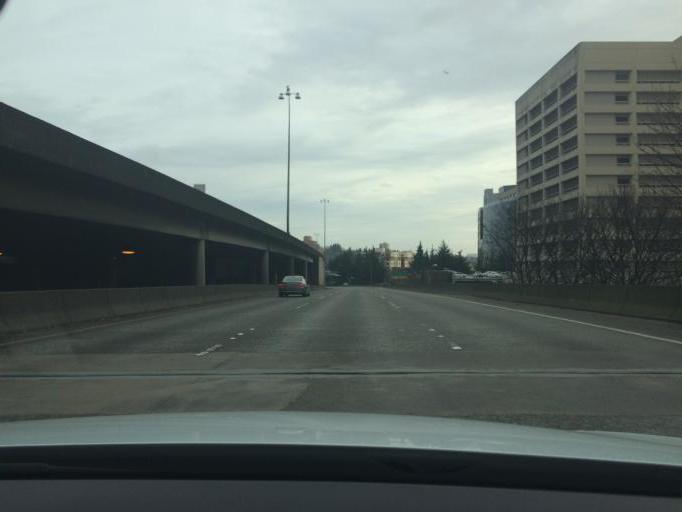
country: US
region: Washington
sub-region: King County
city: Seattle
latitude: 47.6048
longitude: -122.3284
